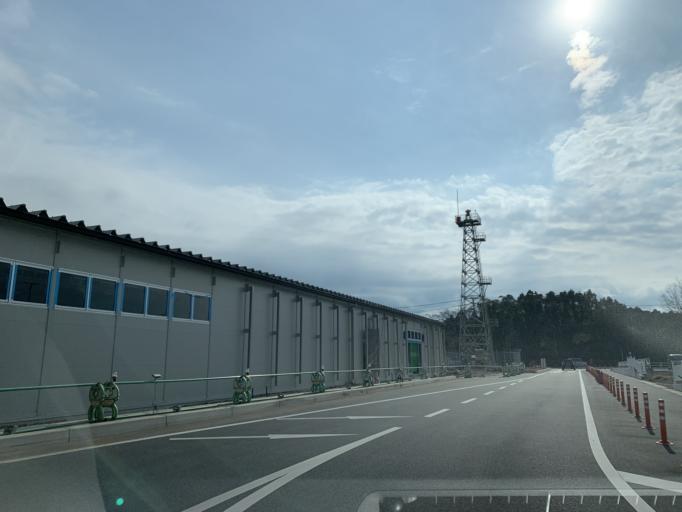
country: JP
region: Kumamoto
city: Ozu
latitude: 32.8349
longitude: 130.8609
